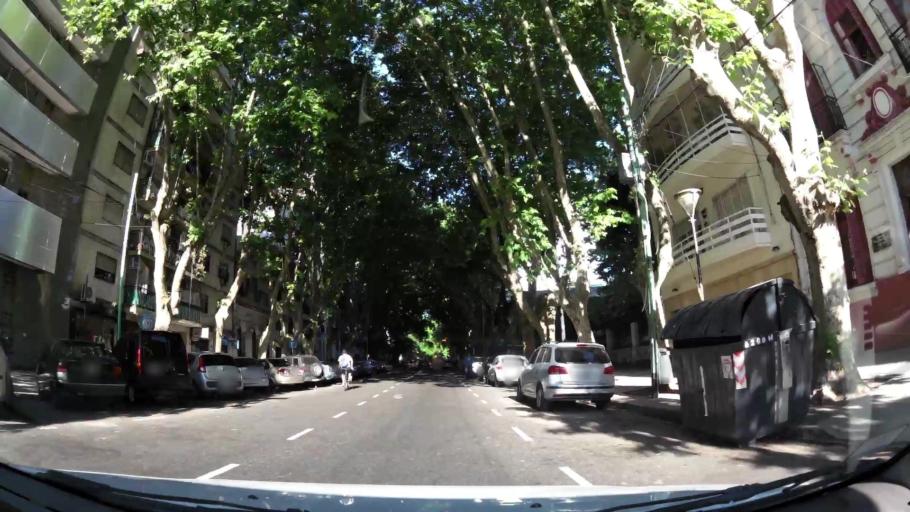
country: AR
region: Buenos Aires F.D.
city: Colegiales
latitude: -34.6149
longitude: -58.4269
